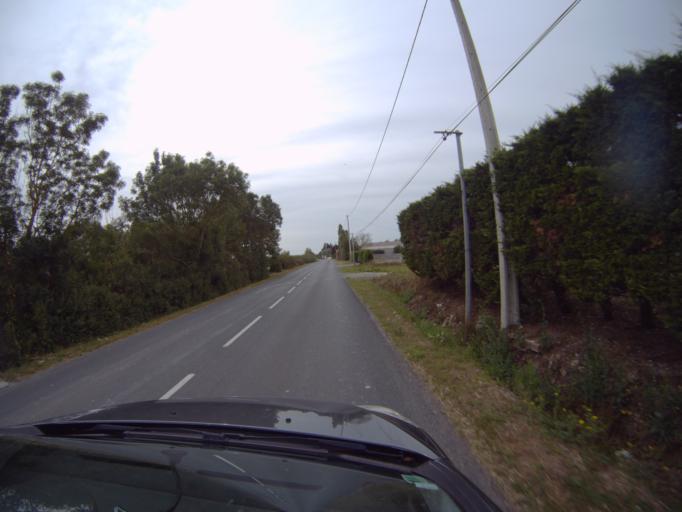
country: FR
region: Pays de la Loire
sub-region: Departement de la Vendee
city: Triaize
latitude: 46.3896
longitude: -1.1879
